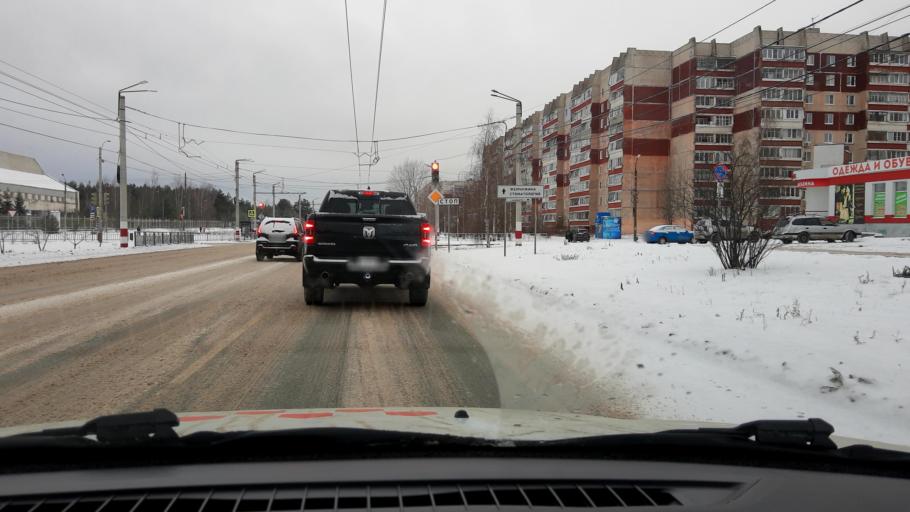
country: RU
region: Nizjnij Novgorod
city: Dzerzhinsk
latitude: 56.2269
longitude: 43.3850
